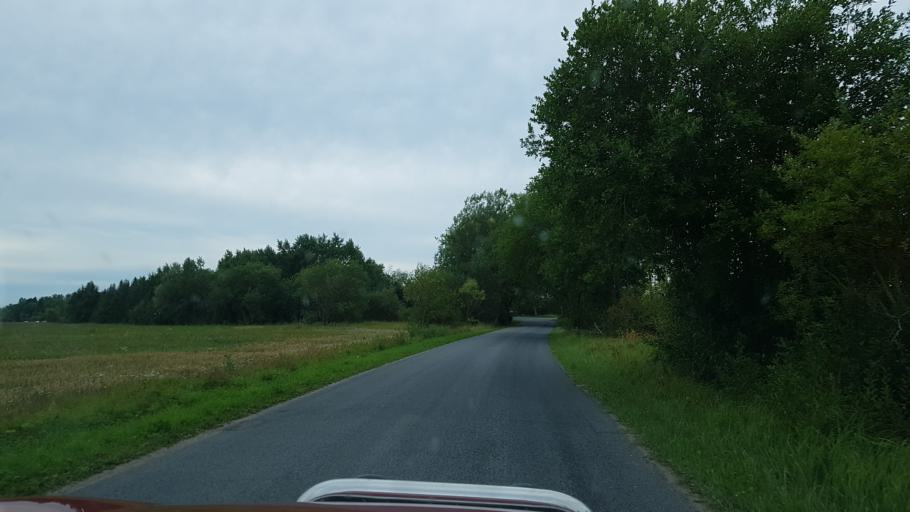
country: EE
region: Laeaene
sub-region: Ridala Parish
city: Uuemoisa
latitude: 58.8085
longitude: 23.6731
